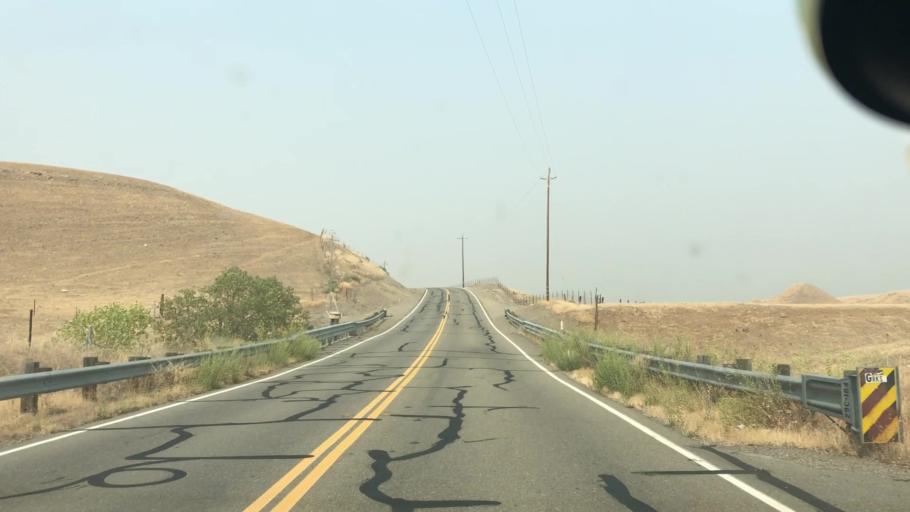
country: US
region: California
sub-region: San Joaquin County
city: Tracy
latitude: 37.6627
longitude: -121.4688
